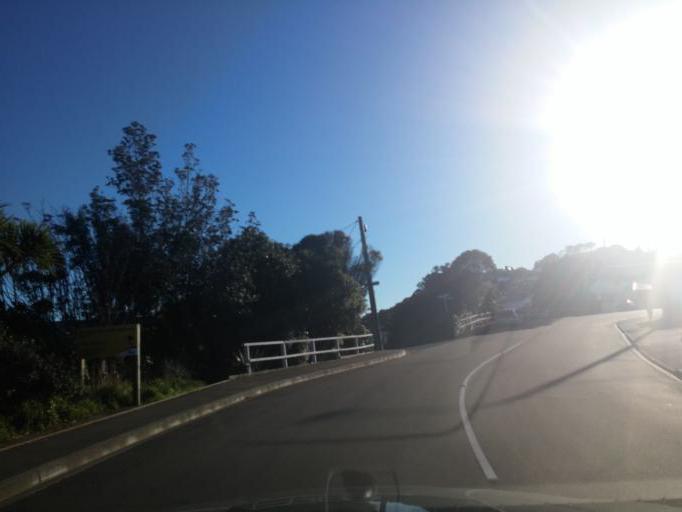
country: NZ
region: Wellington
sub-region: Wellington City
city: Kelburn
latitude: -41.2822
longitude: 174.7583
